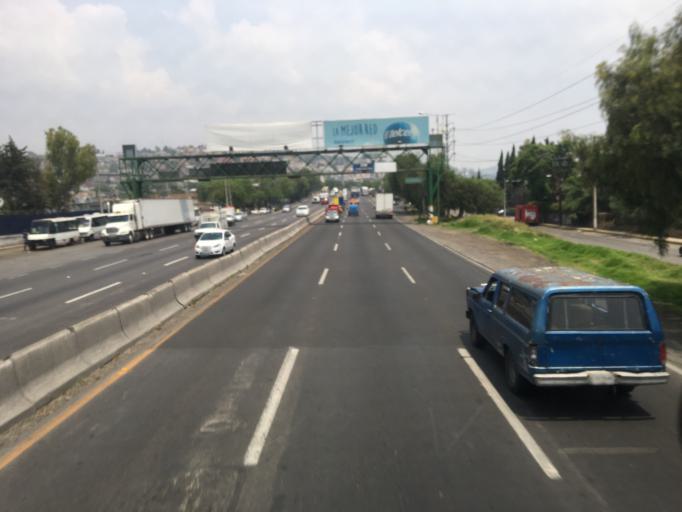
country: MX
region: Mexico
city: Tlalnepantla
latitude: 19.5615
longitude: -99.2004
